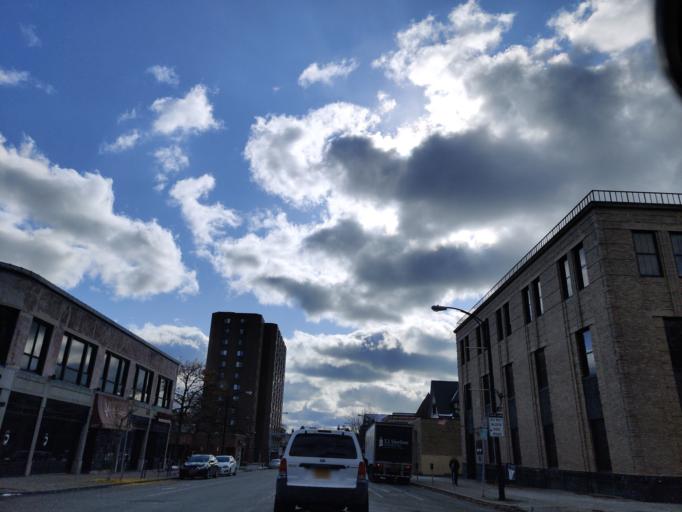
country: US
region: New York
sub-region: Erie County
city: Buffalo
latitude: 42.9124
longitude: -78.8771
